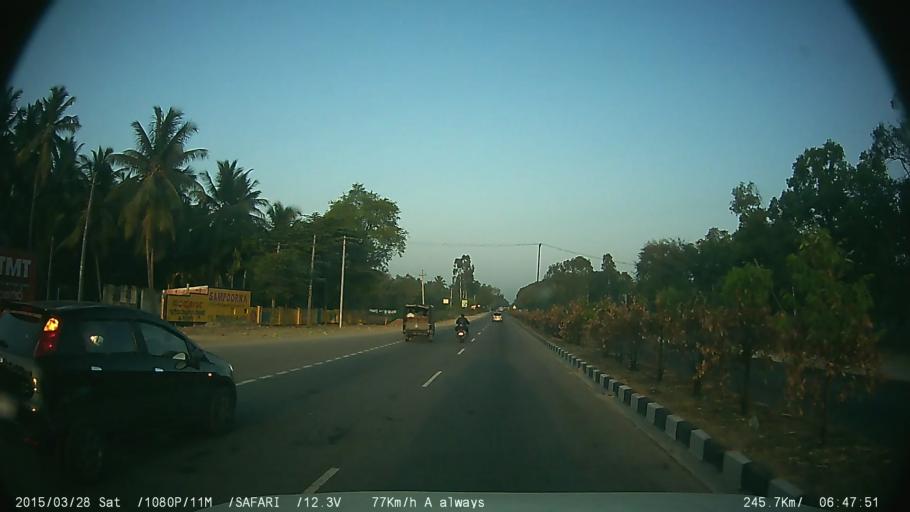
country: IN
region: Karnataka
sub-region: Mandya
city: Maddur
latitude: 12.6132
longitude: 77.0733
